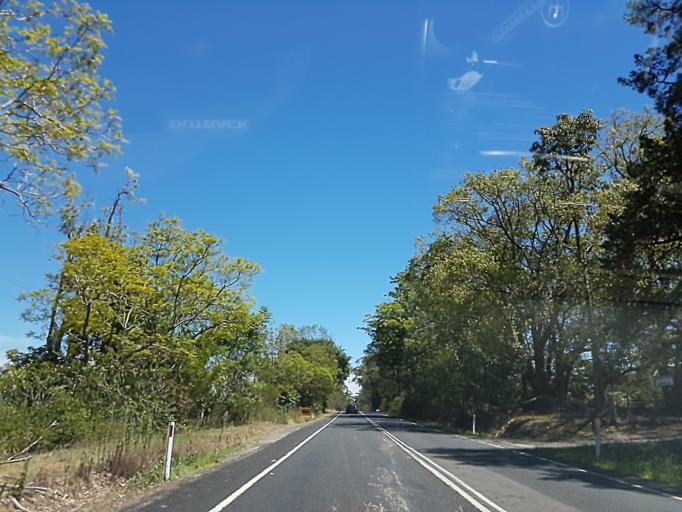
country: AU
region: New South Wales
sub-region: Hornsby Shire
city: Glenorie
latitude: -33.4860
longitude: 151.0124
